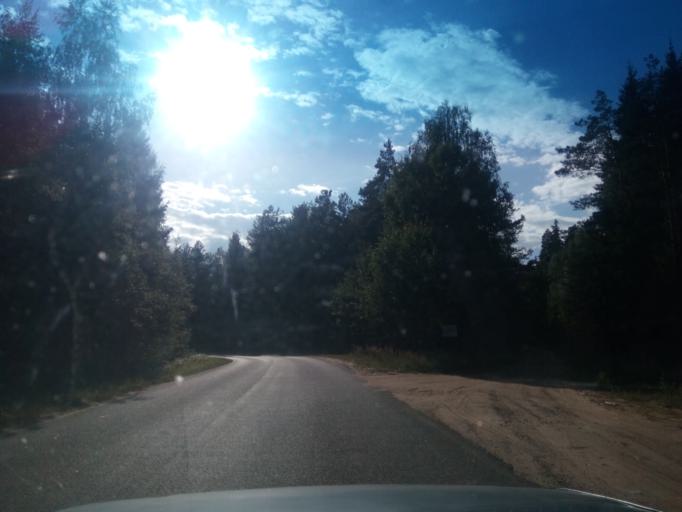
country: BY
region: Vitebsk
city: Polatsk
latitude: 55.4279
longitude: 28.7619
